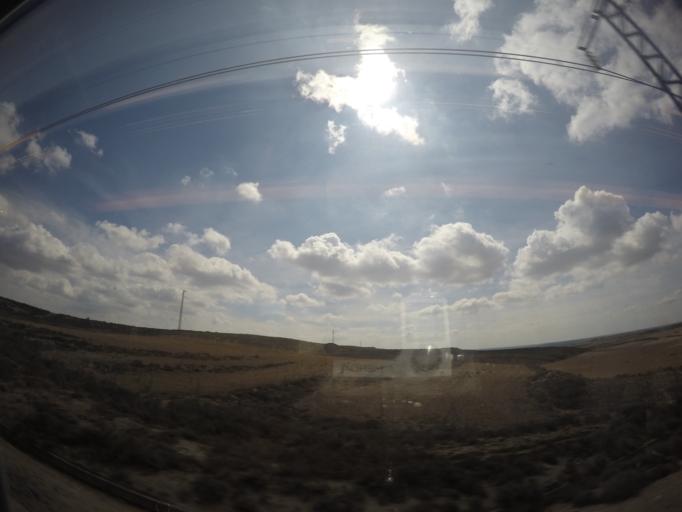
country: ES
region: Aragon
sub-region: Provincia de Huesca
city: Candasnos
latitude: 41.5661
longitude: 0.0922
